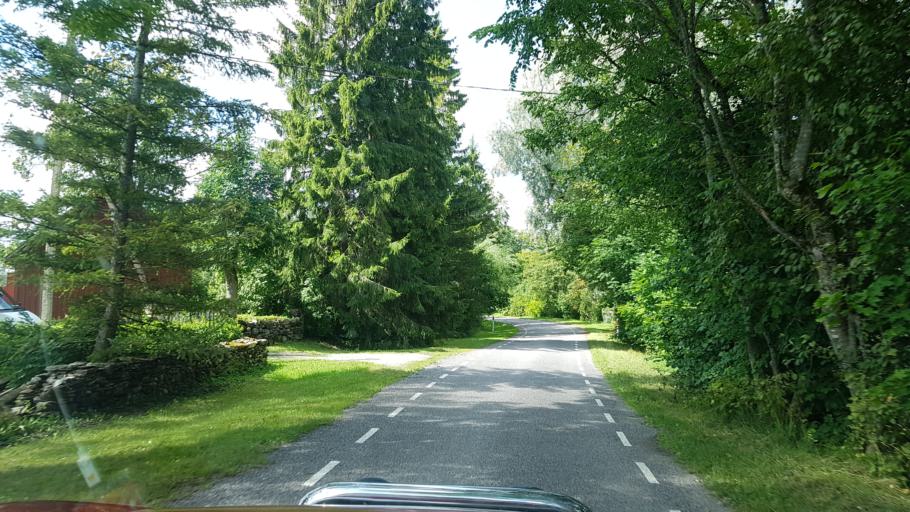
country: EE
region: Raplamaa
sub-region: Rapla vald
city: Rapla
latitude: 58.9683
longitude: 24.6289
